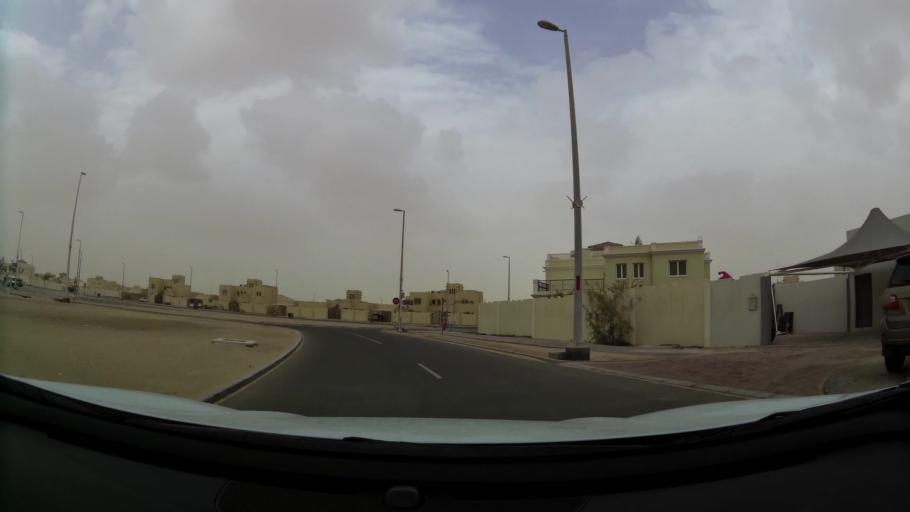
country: AE
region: Abu Dhabi
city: Abu Dhabi
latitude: 24.4470
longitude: 54.7169
